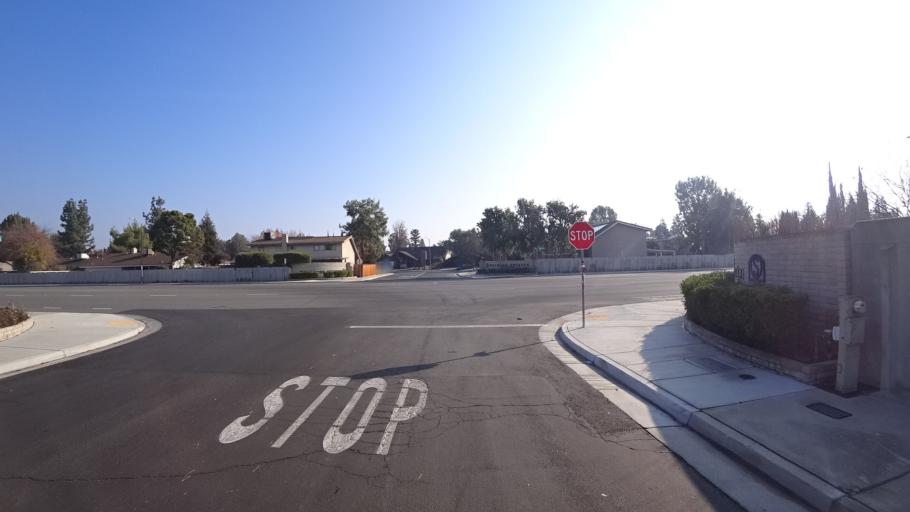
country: US
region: California
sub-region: Kern County
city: Greenacres
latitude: 35.3419
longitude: -119.0748
